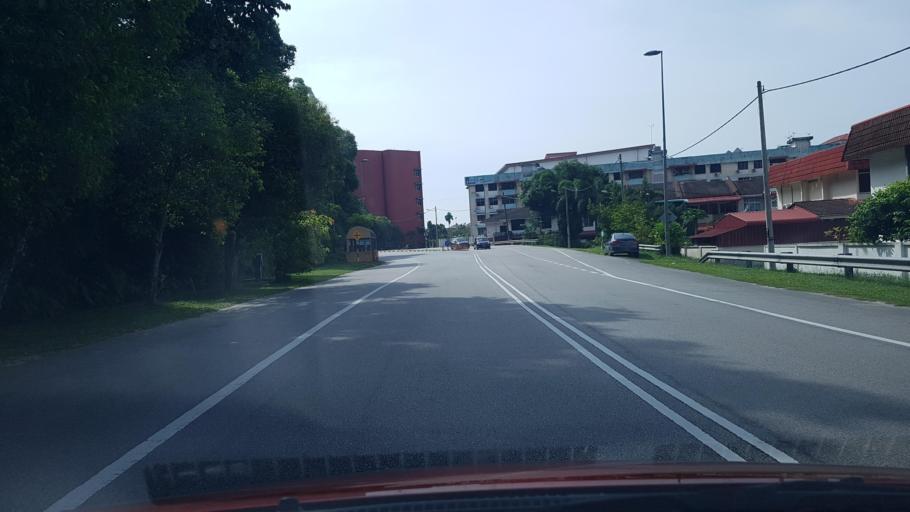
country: MY
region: Terengganu
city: Kuala Terengganu
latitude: 5.3235
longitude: 103.1380
